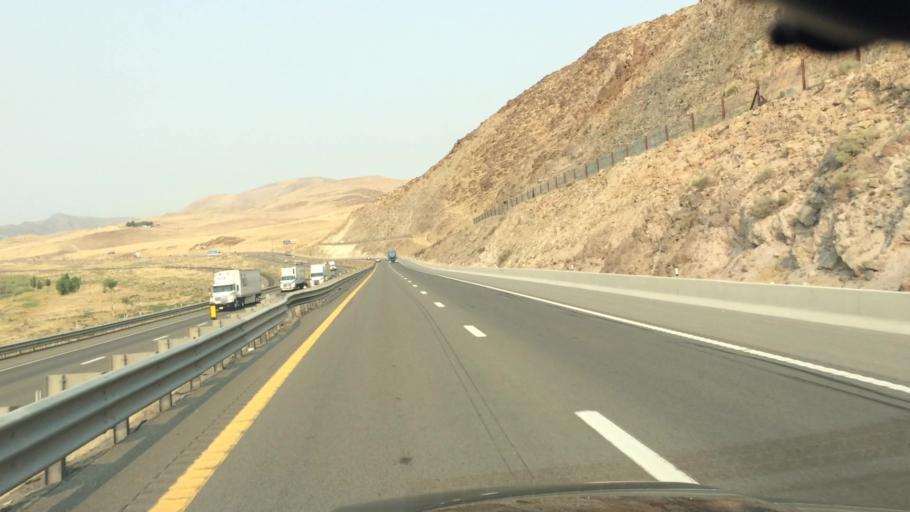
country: US
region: Nevada
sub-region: Washoe County
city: Spanish Springs
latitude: 39.5483
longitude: -119.5817
